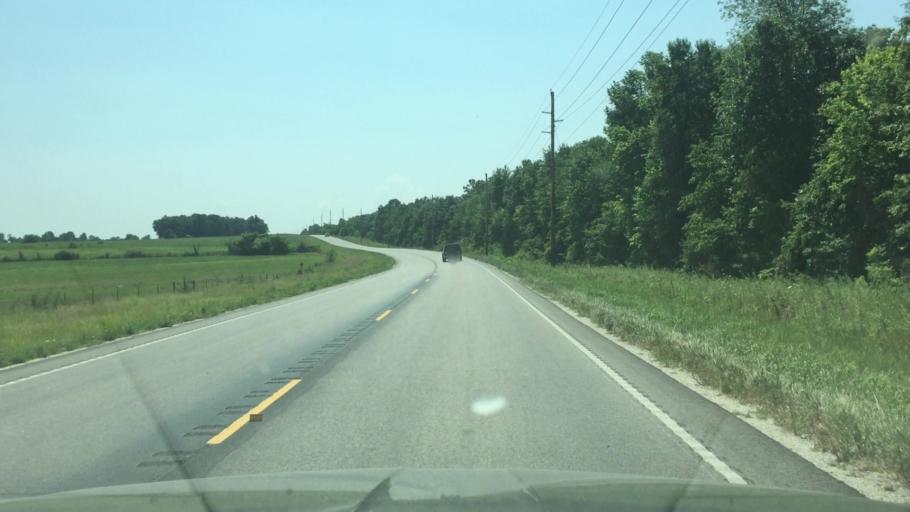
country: US
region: Missouri
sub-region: Miller County
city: Eldon
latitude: 38.3900
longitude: -92.7049
